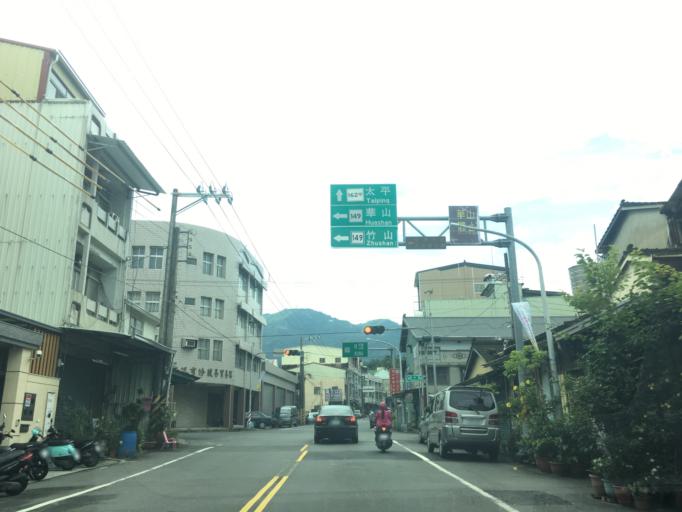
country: TW
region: Taiwan
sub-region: Yunlin
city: Douliu
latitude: 23.5838
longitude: 120.5596
